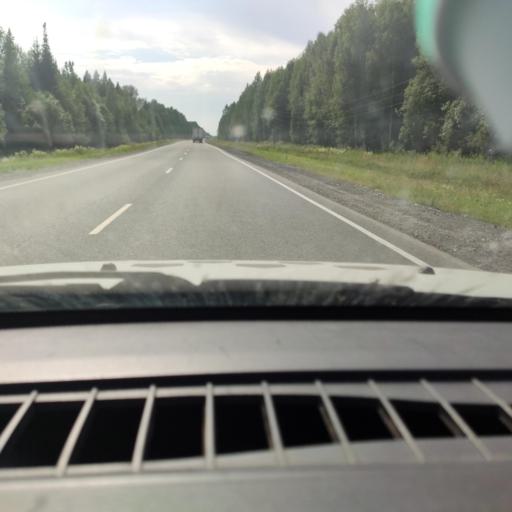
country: RU
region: Kirov
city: Kostino
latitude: 58.8285
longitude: 53.0076
